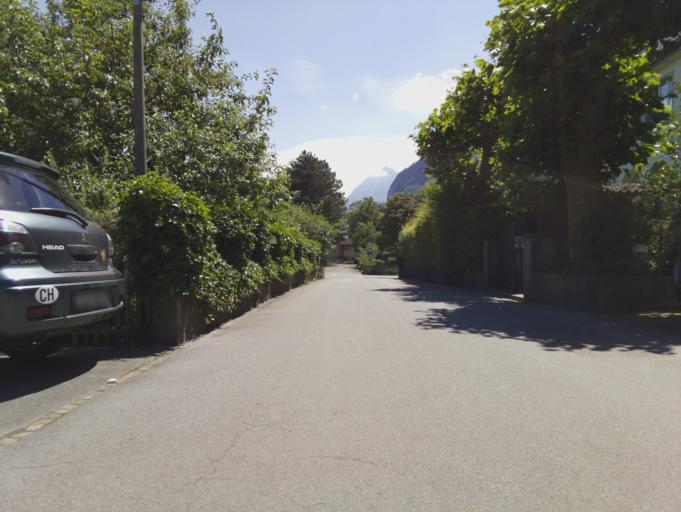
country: CH
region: Glarus
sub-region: Glarus
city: Niederurnen
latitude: 47.1250
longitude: 9.0584
